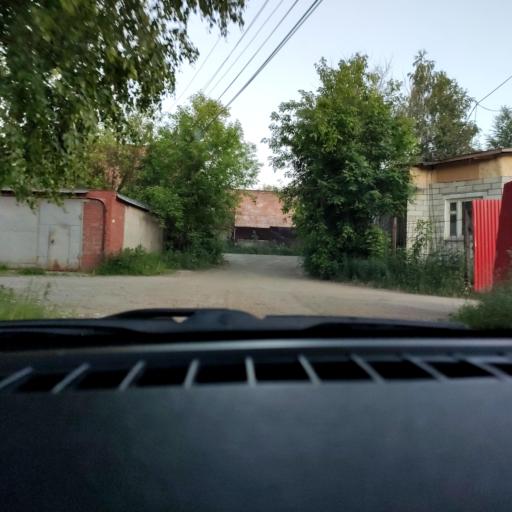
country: RU
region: Perm
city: Perm
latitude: 58.0724
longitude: 56.3558
